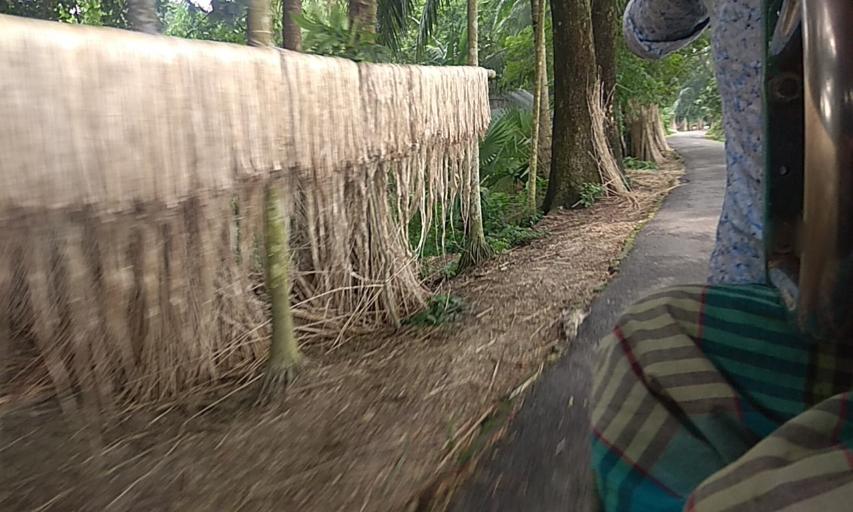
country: BD
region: Dhaka
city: Dohar
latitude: 23.4746
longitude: 90.0600
